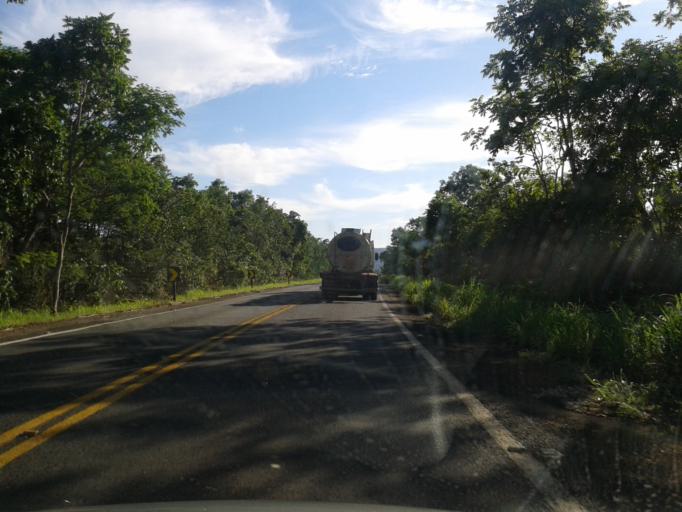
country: BR
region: Minas Gerais
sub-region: Tupaciguara
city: Tupaciguara
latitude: -18.2127
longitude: -48.5714
